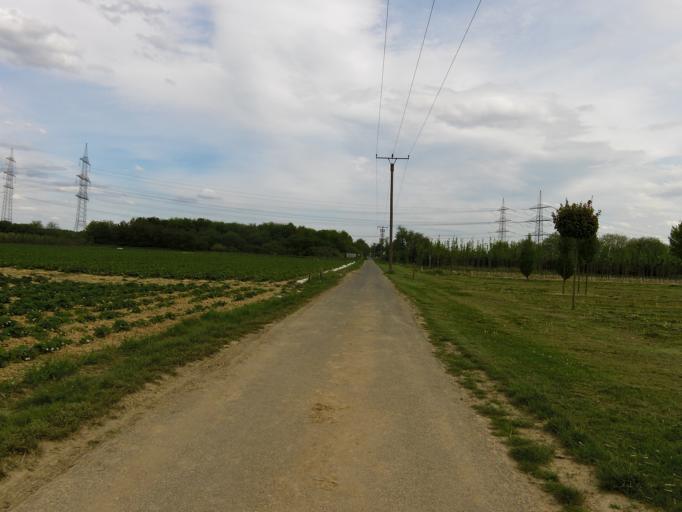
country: DE
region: North Rhine-Westphalia
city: Meckenheim
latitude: 50.6297
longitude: 7.0040
